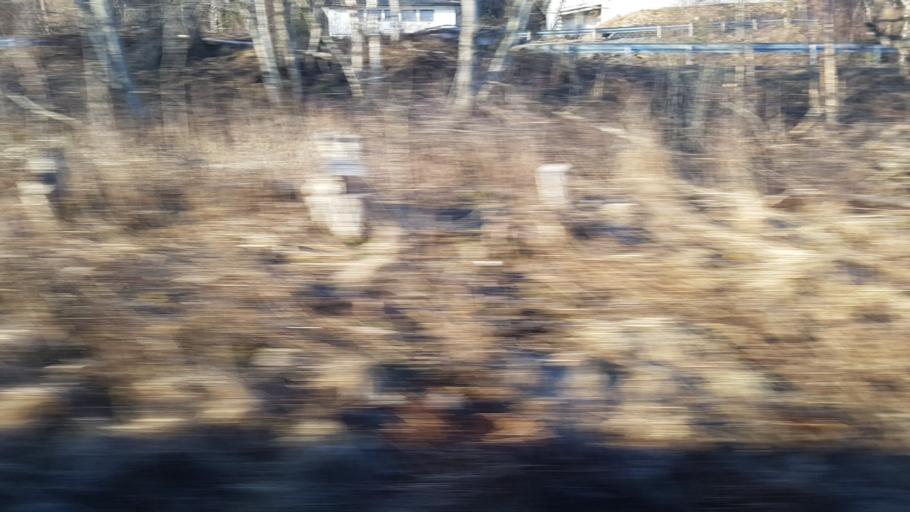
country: NO
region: Sor-Trondelag
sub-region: Malvik
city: Hommelvik
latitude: 63.4265
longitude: 10.7607
